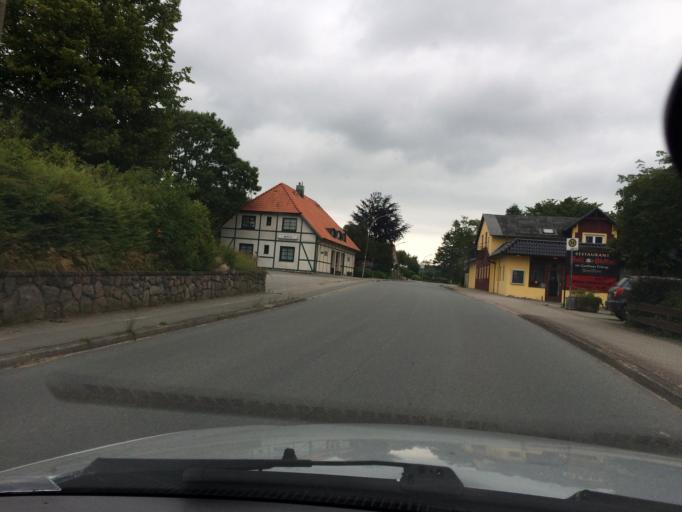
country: DE
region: Schleswig-Holstein
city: Oeversee
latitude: 54.6954
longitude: 9.4276
